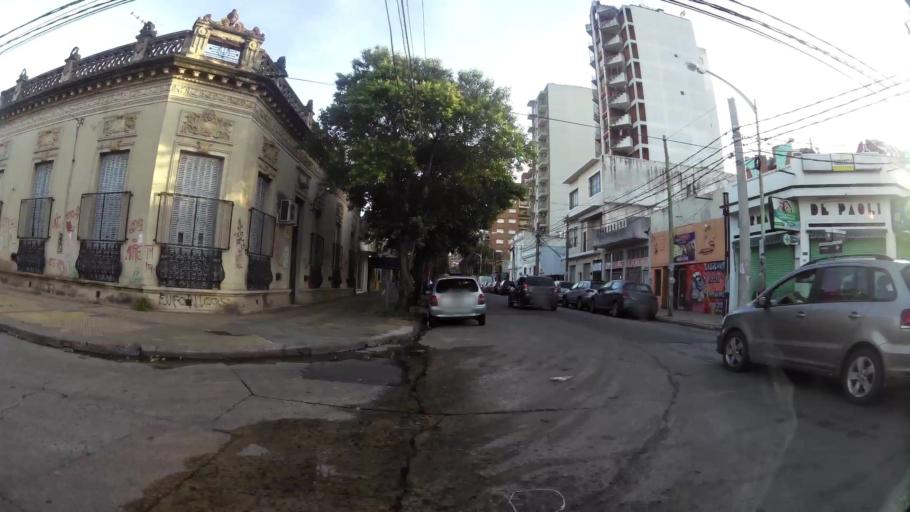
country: AR
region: Buenos Aires
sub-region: Partido de Moron
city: Moron
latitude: -34.6455
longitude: -58.6226
